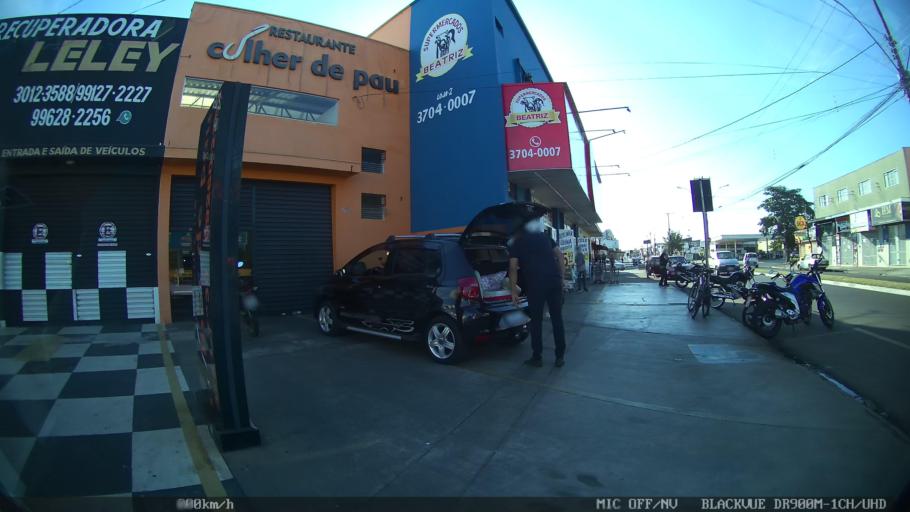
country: BR
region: Sao Paulo
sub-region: Franca
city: Franca
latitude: -20.5179
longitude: -47.3719
